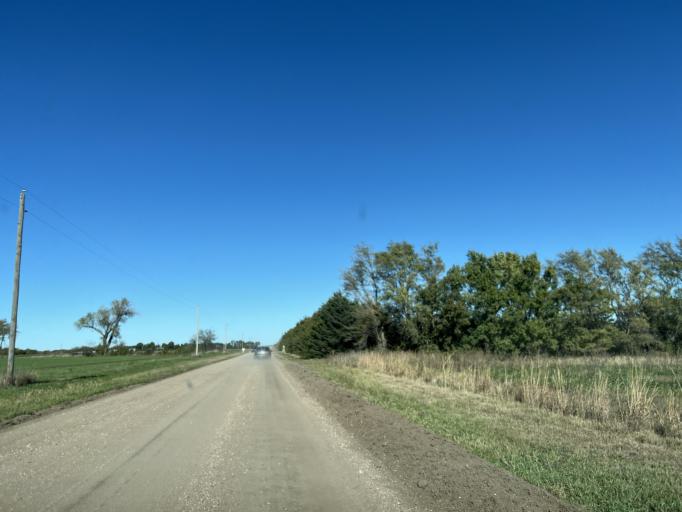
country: US
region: Kansas
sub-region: McPherson County
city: Moundridge
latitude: 38.2099
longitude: -97.6292
